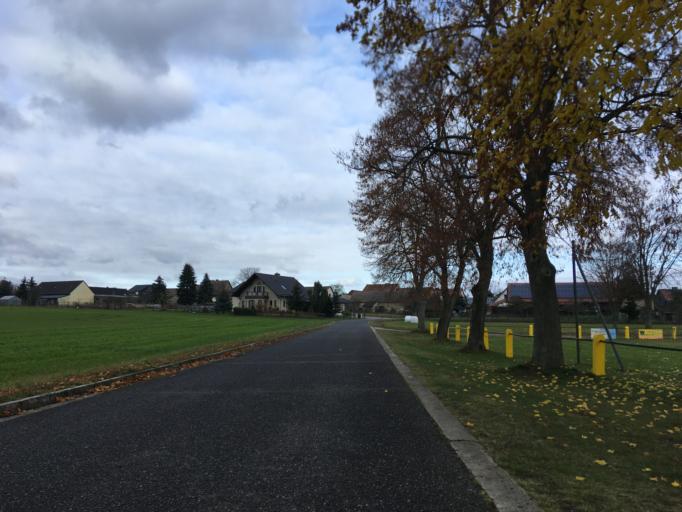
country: DE
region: Brandenburg
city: Schenkendobern
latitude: 51.9796
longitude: 14.5331
